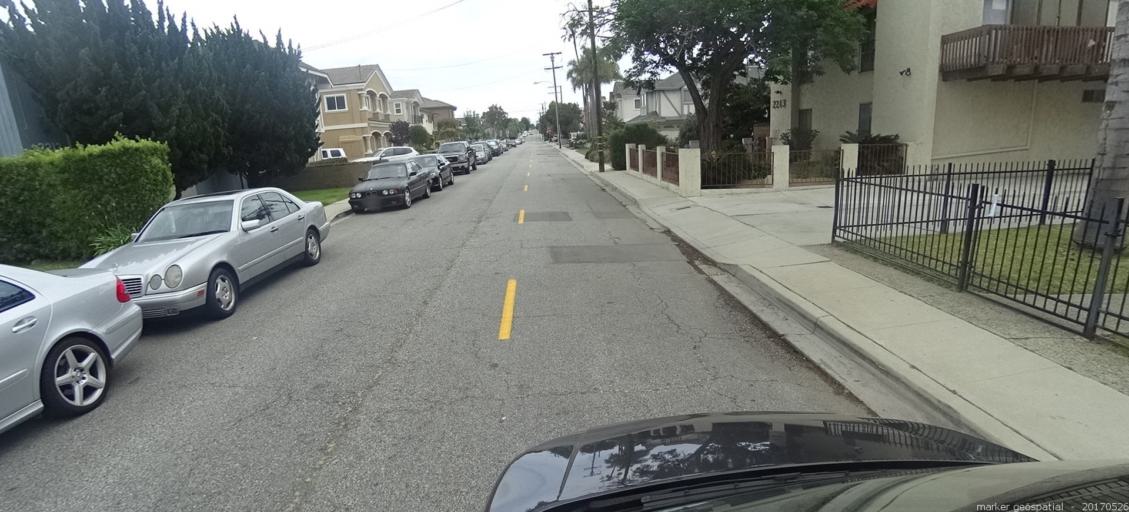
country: US
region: California
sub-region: Los Angeles County
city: Lawndale
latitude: 33.8766
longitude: -118.3714
